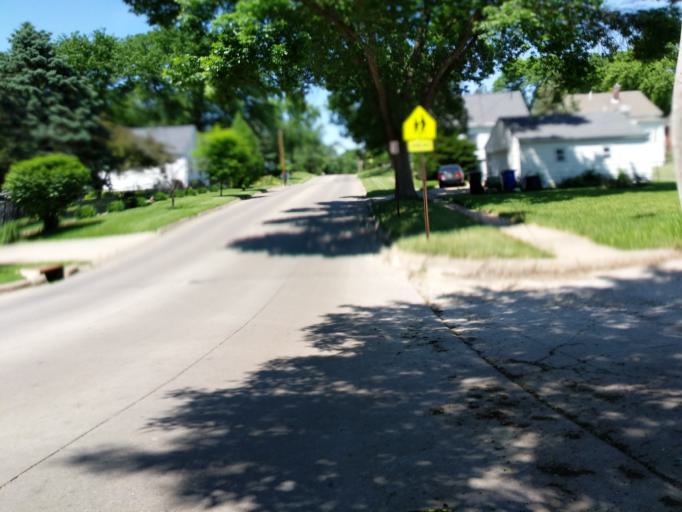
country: US
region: Iowa
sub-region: Linn County
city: Cedar Rapids
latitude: 42.0140
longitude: -91.6385
